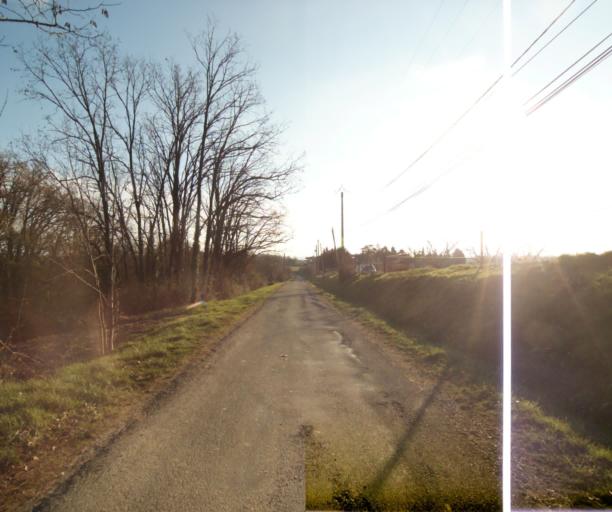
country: FR
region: Midi-Pyrenees
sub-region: Departement du Tarn-et-Garonne
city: Moissac
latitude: 44.1382
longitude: 1.1377
